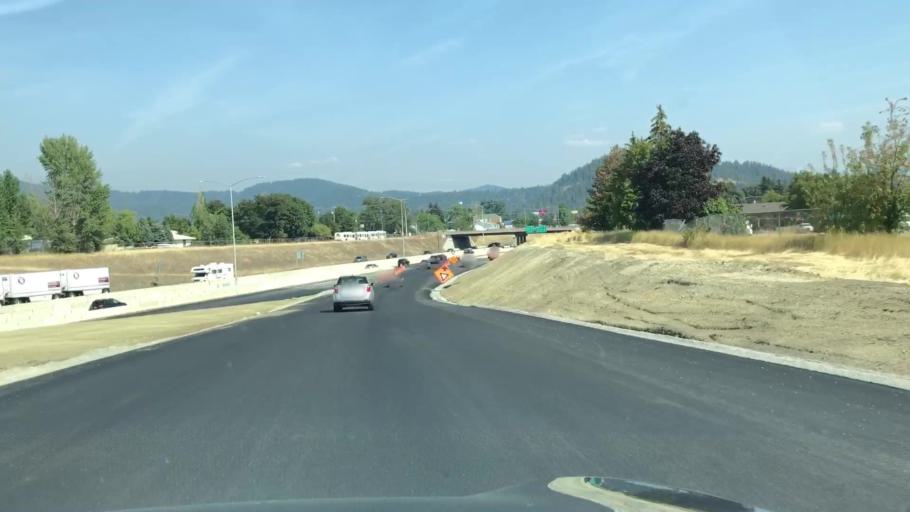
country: US
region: Idaho
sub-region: Kootenai County
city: Coeur d'Alene
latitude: 47.6982
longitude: -116.7907
